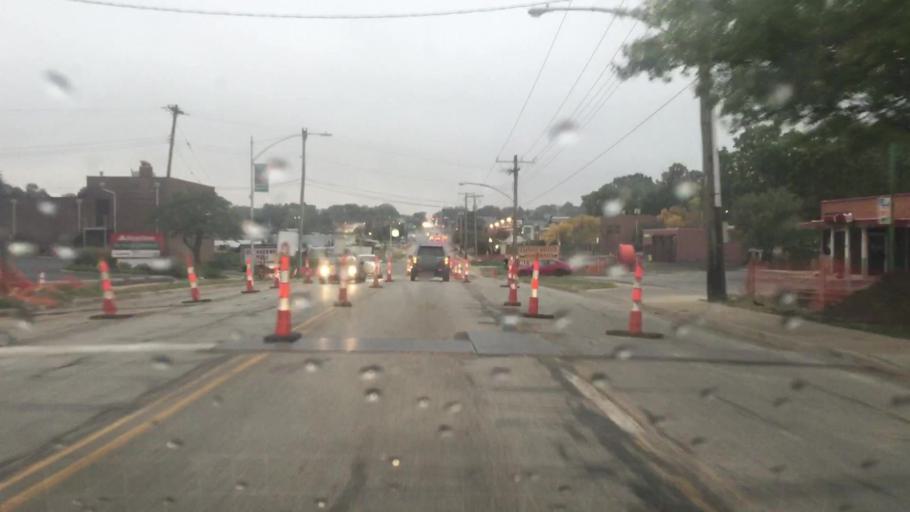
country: US
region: Kansas
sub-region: Johnson County
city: Merriam
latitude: 39.0200
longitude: -94.7146
